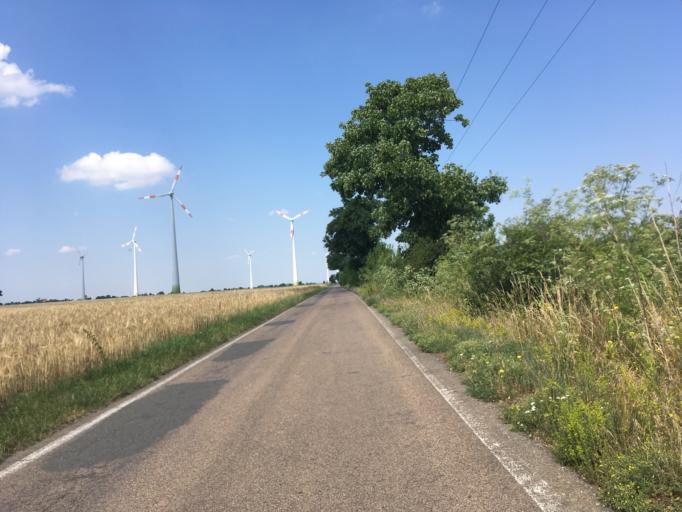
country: DE
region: Saxony-Anhalt
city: Quellendorf
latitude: 51.7834
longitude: 12.1401
